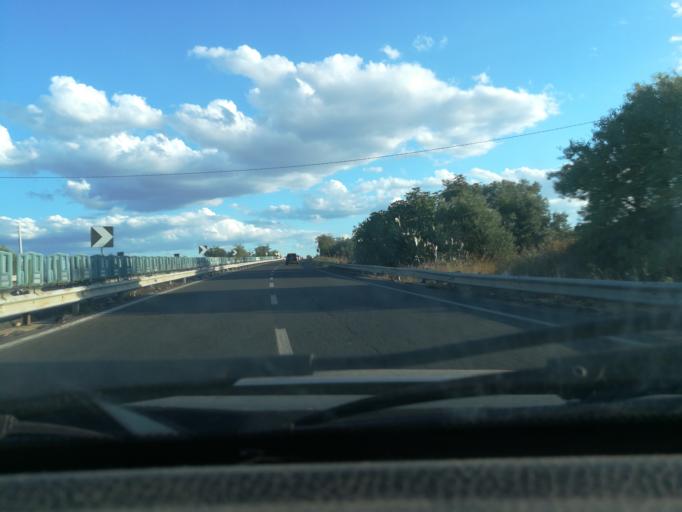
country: IT
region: Apulia
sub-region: Provincia di Bari
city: Mola di Bari
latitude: 41.0673
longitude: 17.0666
